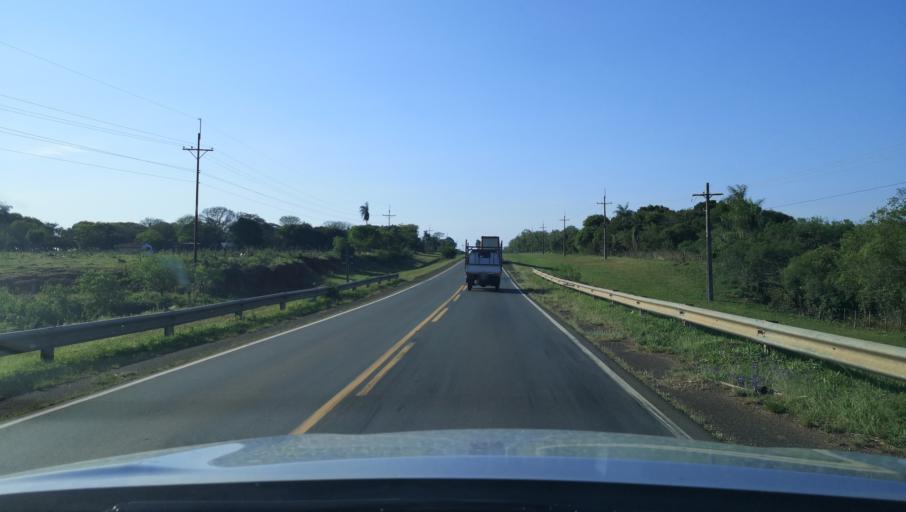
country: PY
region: Misiones
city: Santa Maria
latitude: -26.7701
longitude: -57.0309
